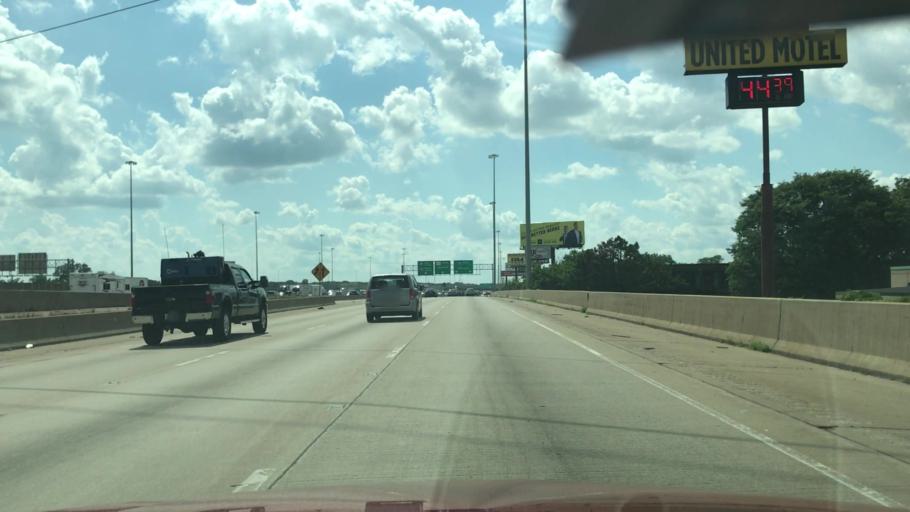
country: US
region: Illinois
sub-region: Cook County
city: Lansing
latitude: 41.5782
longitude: -87.5619
